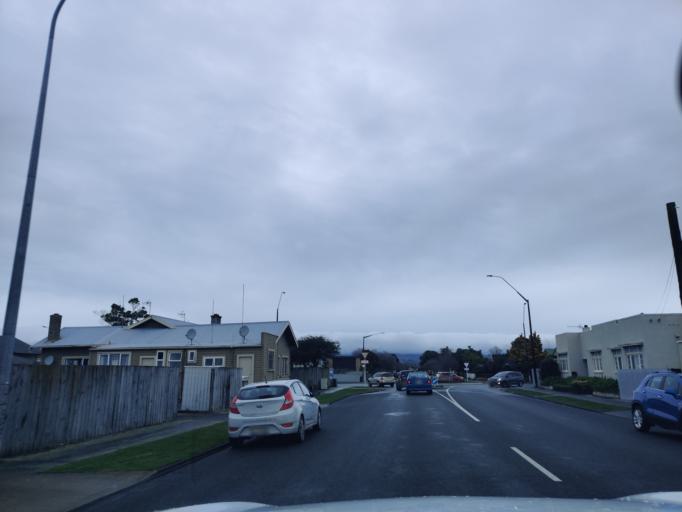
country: NZ
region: Manawatu-Wanganui
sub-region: Palmerston North City
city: Palmerston North
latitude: -40.3446
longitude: 175.6163
